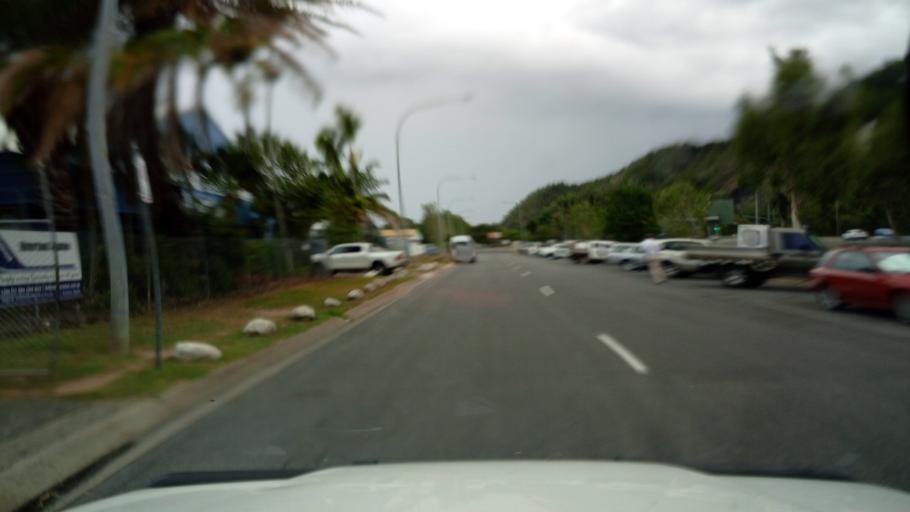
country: AU
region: Queensland
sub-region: Cairns
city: Cairns
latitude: -16.8816
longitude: 145.7463
